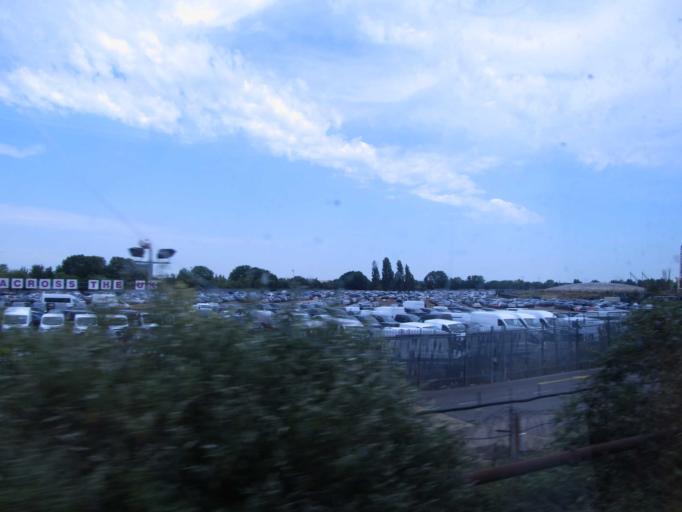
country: GB
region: England
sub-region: Greater London
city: Southall
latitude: 51.5036
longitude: -0.3973
